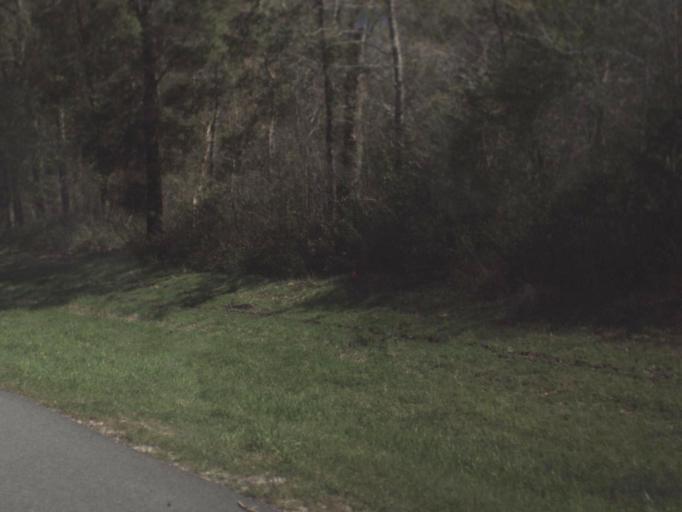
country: US
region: Florida
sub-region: Gadsden County
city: Quincy
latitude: 30.4761
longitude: -84.6280
